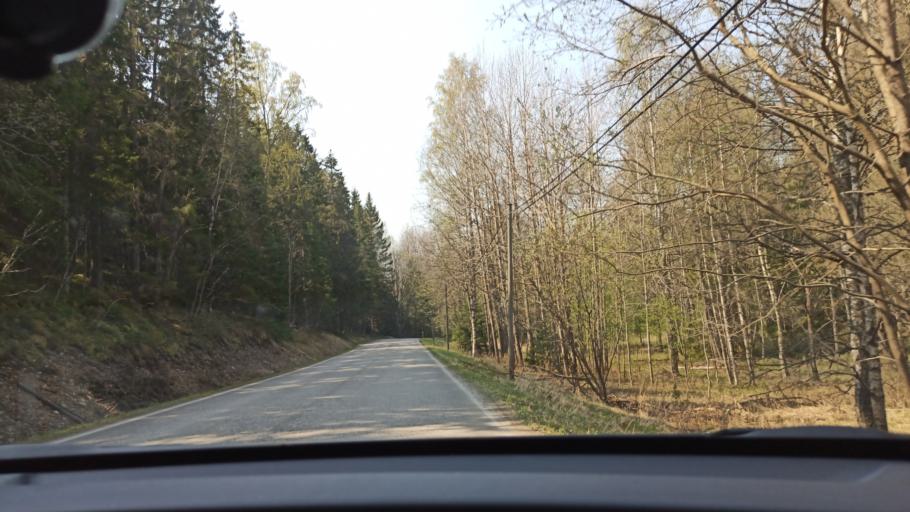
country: FI
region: Uusimaa
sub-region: Helsinki
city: Espoo
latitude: 60.0940
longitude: 24.5788
